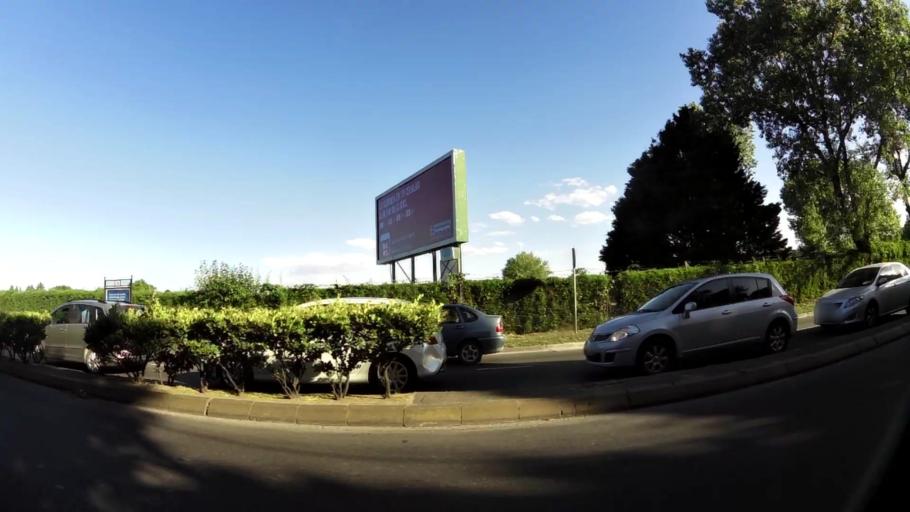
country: AR
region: Buenos Aires
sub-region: Partido de San Isidro
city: San Isidro
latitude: -34.4878
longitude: -58.5387
